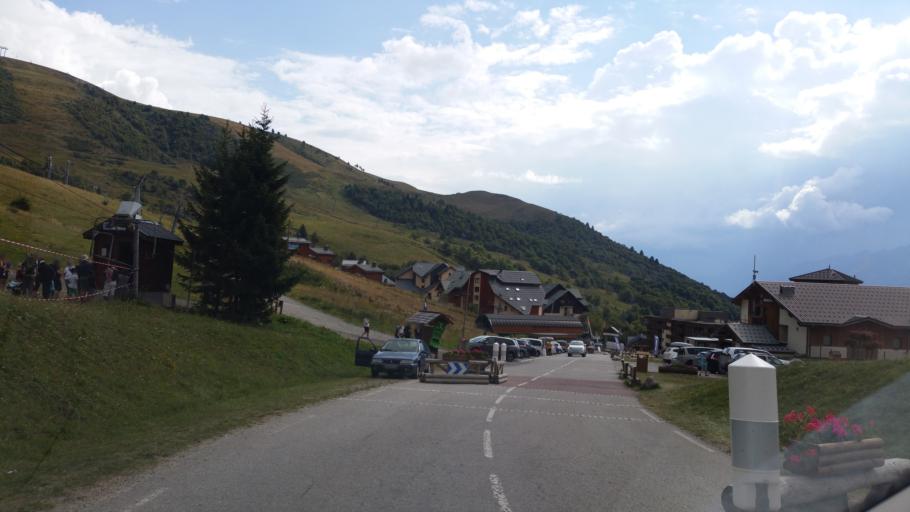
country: FR
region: Rhone-Alpes
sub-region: Departement de la Savoie
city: La Chambre
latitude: 45.4186
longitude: 6.3650
